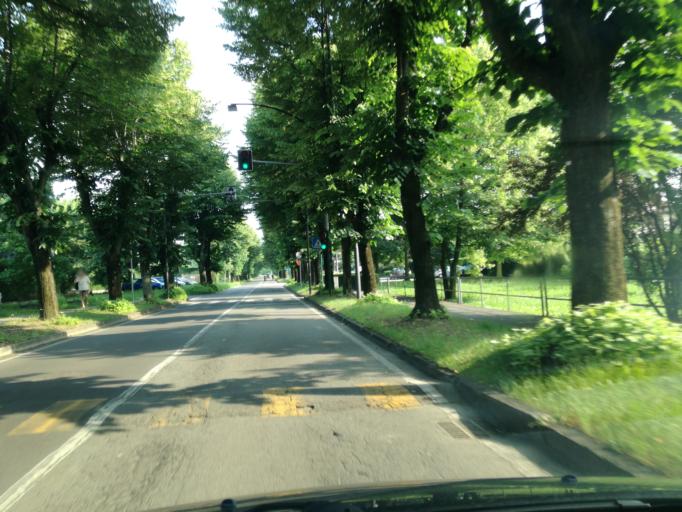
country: IT
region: Lombardy
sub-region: Provincia di Lecco
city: Paderno d'Adda
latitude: 45.6767
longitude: 9.4401
